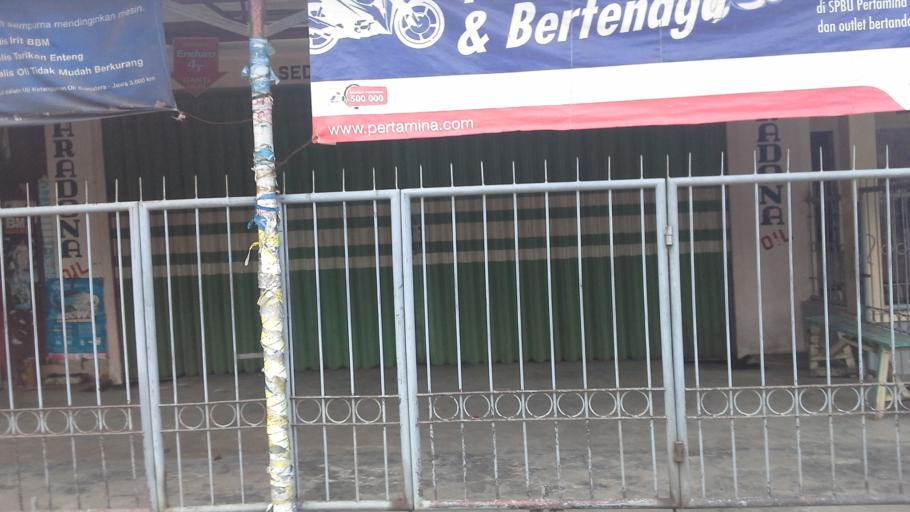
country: ID
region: East Java
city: Bondowoso
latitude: -7.9086
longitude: 113.8531
